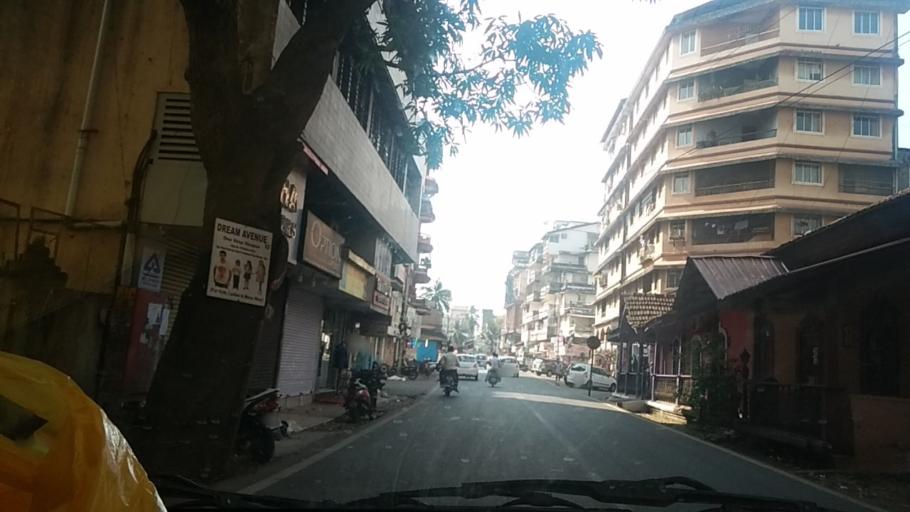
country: IN
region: Goa
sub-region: South Goa
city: Madgaon
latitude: 15.2717
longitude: 73.9636
